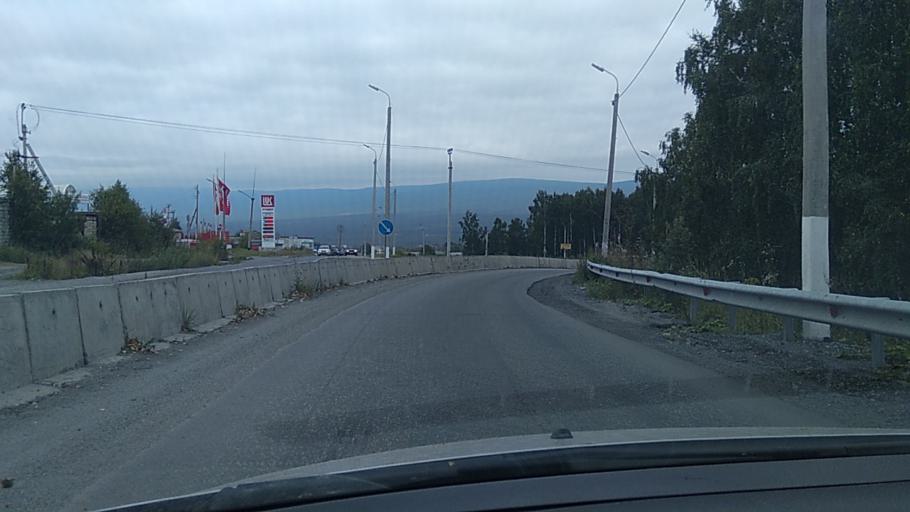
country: RU
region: Chelyabinsk
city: Zlatoust
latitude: 55.1166
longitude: 59.7366
